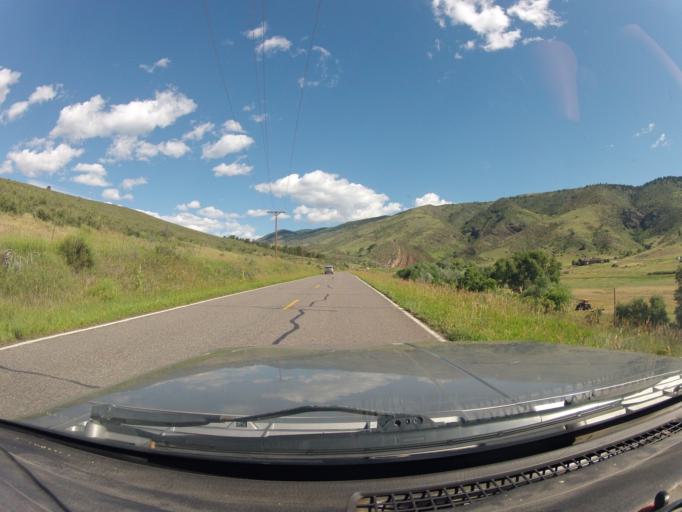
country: US
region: Colorado
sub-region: Larimer County
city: Laporte
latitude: 40.5043
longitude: -105.2280
